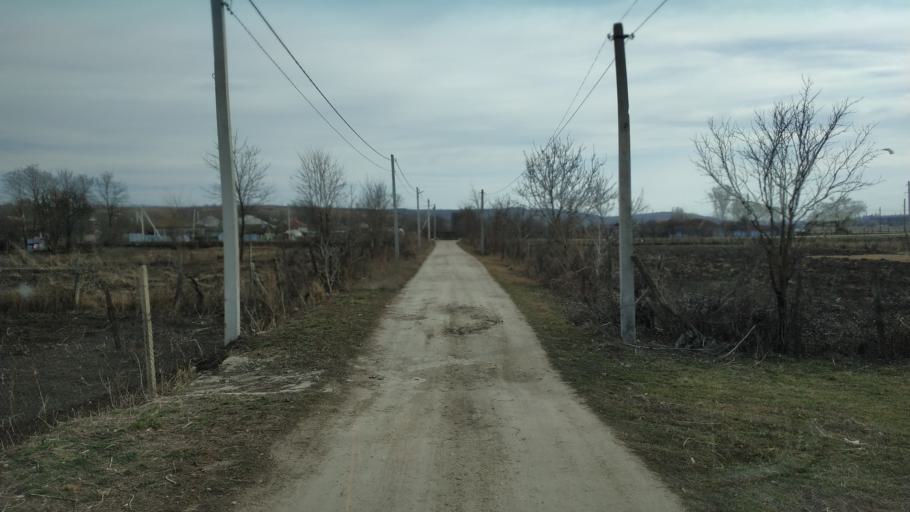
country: RO
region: Vaslui
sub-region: Comuna Dranceni
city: Dranceni
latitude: 46.8750
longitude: 28.2045
